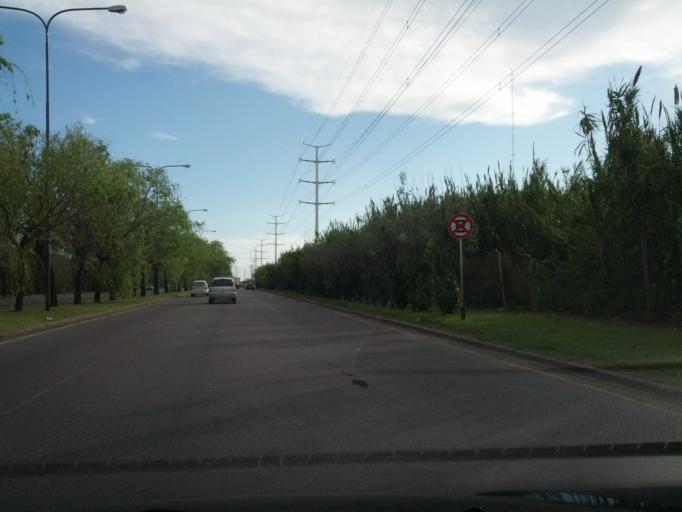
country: AR
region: Buenos Aires F.D.
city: Villa Lugano
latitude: -34.6964
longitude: -58.4542
